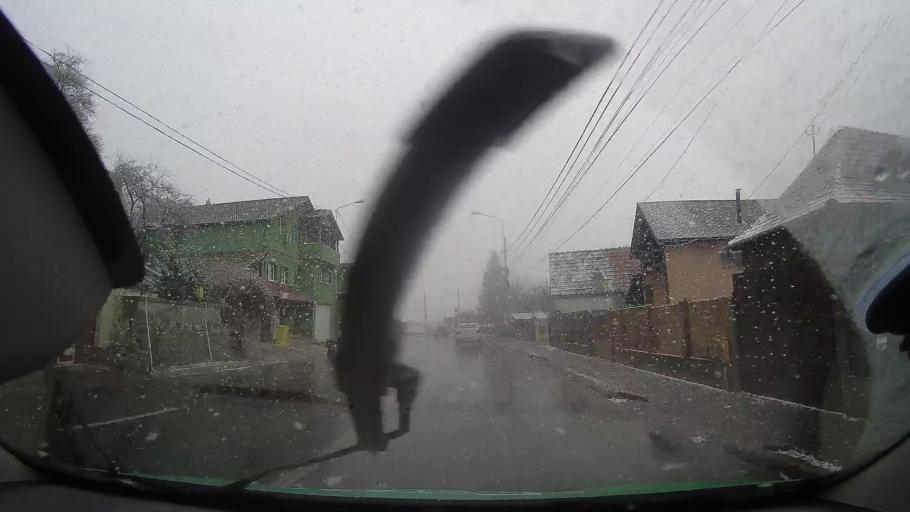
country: RO
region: Sibiu
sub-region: Municipiul Medias
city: Medias
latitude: 46.1728
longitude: 24.3399
